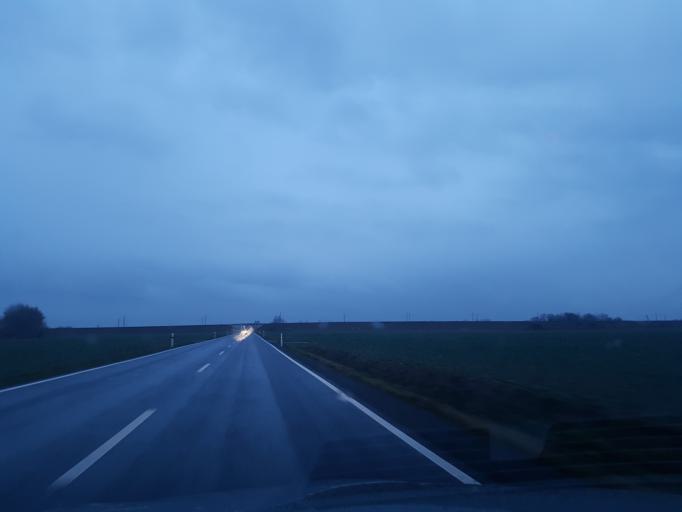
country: DE
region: Saxony
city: Priestewitz
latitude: 51.2714
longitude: 13.5186
